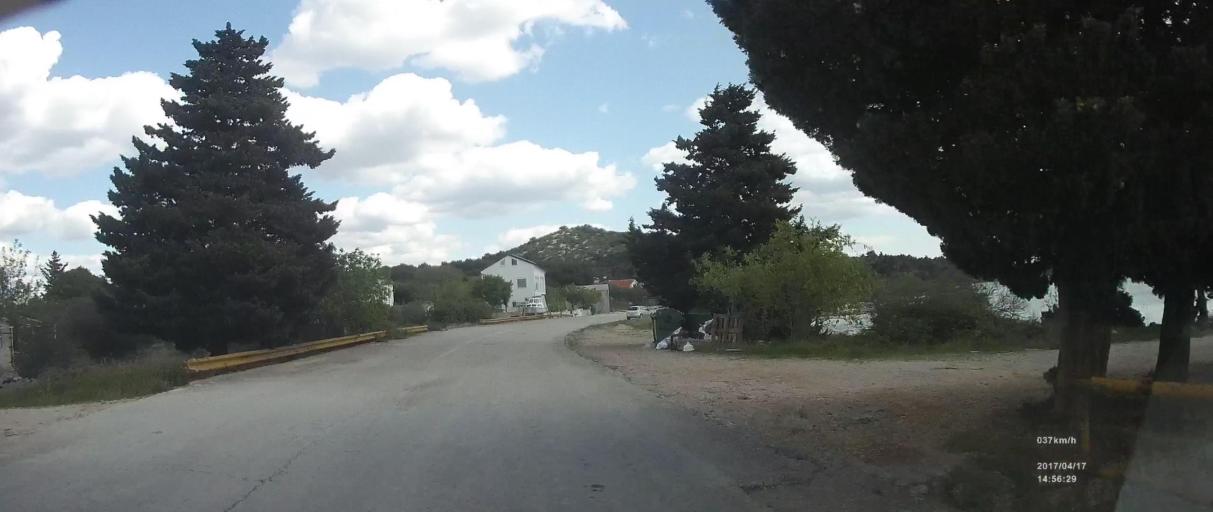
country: HR
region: Sibensko-Kniniska
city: Murter
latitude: 43.8441
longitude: 15.6243
